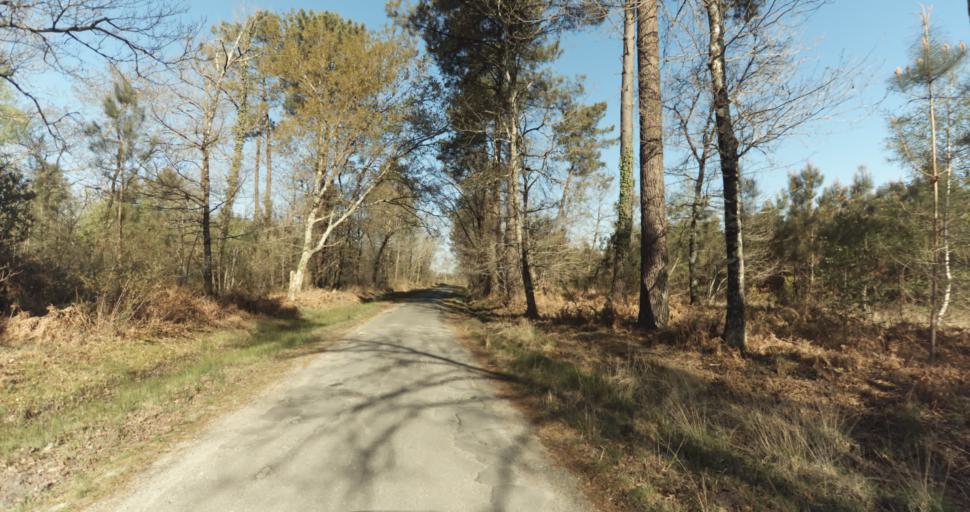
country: FR
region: Aquitaine
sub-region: Departement de la Gironde
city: Martignas-sur-Jalle
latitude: 44.8065
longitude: -0.8466
